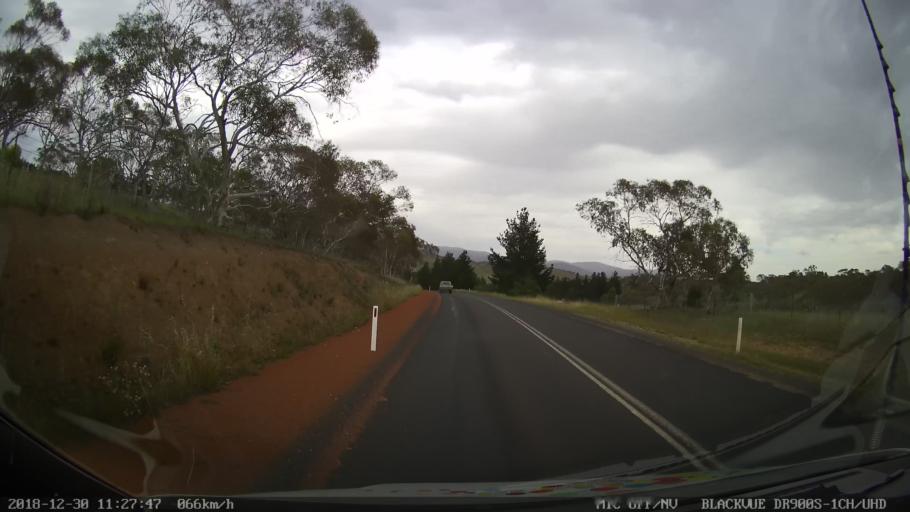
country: AU
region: New South Wales
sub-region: Snowy River
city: Jindabyne
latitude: -36.4575
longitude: 148.6242
